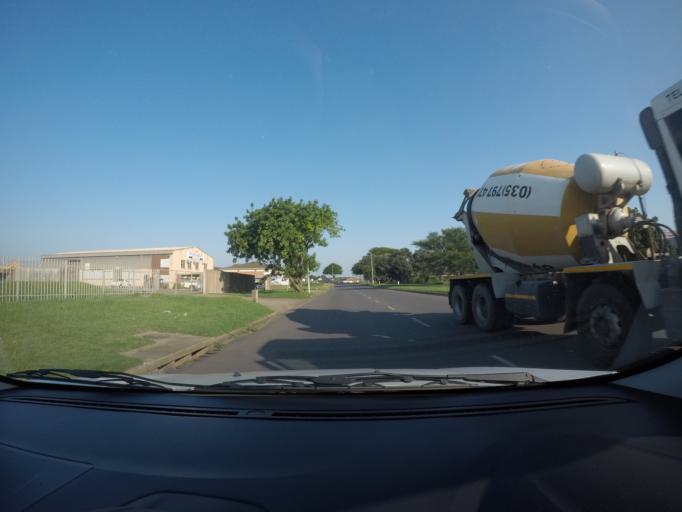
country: ZA
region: KwaZulu-Natal
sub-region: uThungulu District Municipality
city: Richards Bay
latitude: -28.7537
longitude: 32.0234
